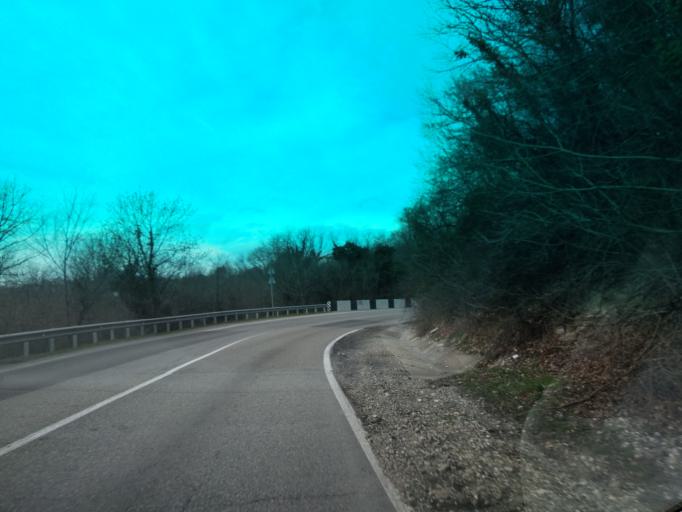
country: RU
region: Krasnodarskiy
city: Tuapse
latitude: 44.0900
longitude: 39.1183
